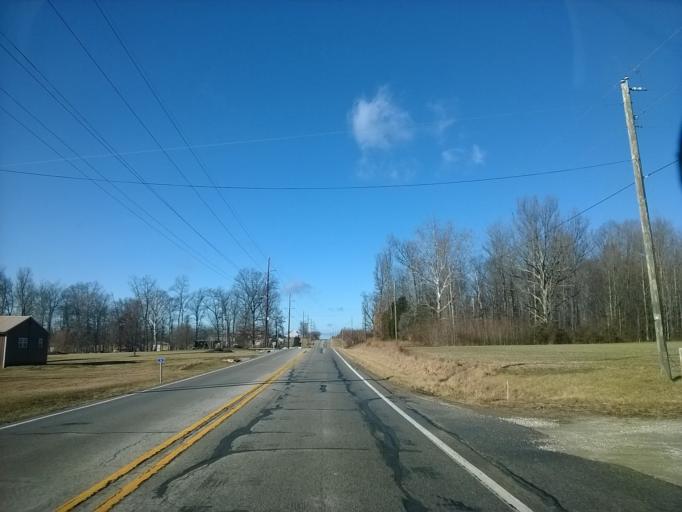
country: US
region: Indiana
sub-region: Scott County
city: Scottsburg
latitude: 38.7368
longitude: -85.6810
